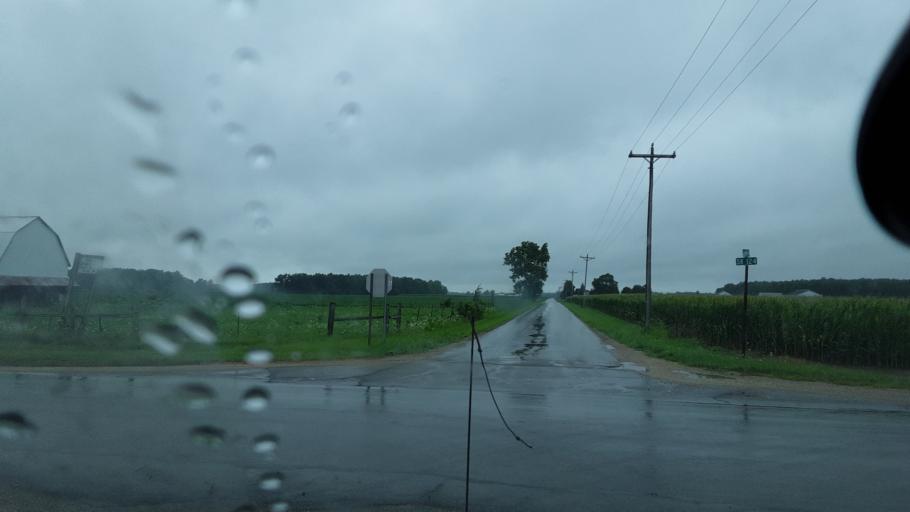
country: US
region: Indiana
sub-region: Adams County
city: Decatur
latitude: 40.7462
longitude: -84.8560
